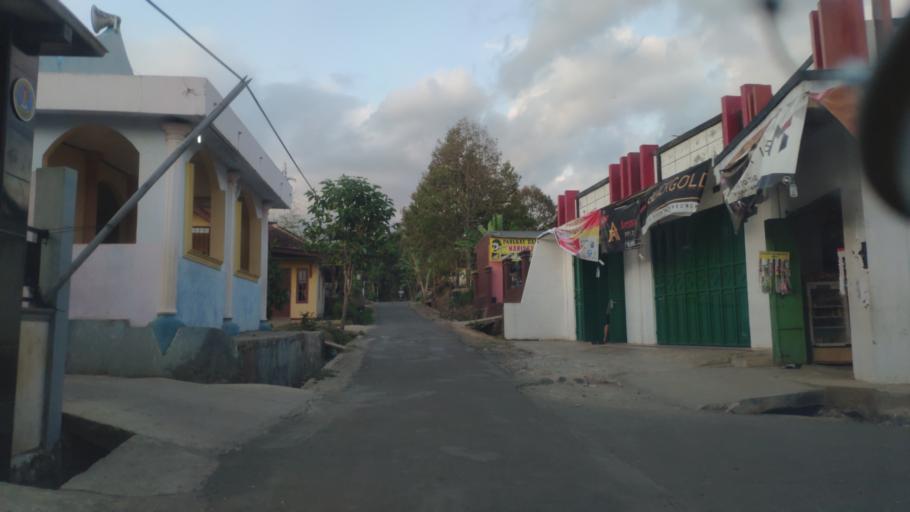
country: ID
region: Central Java
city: Purbalingga
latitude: -7.3556
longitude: 109.5361
